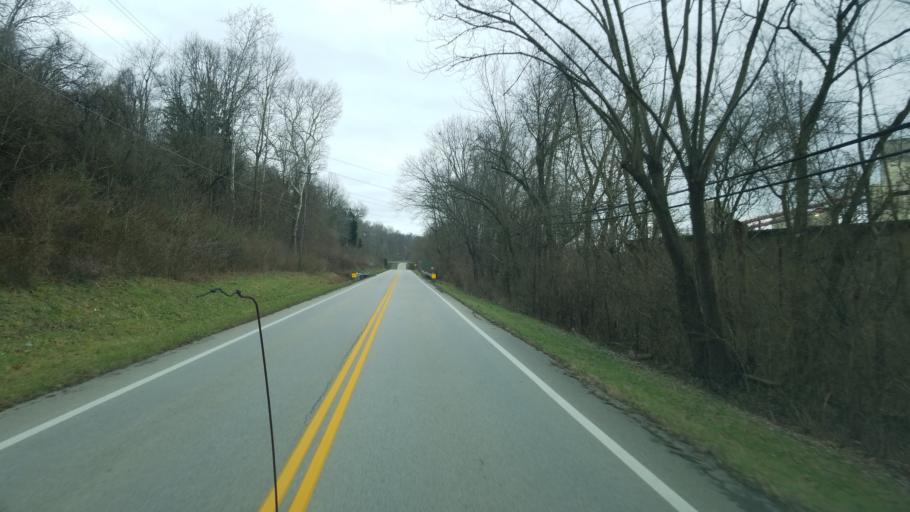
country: US
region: Ohio
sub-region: Clermont County
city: New Richmond
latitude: 38.8720
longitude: -84.2247
